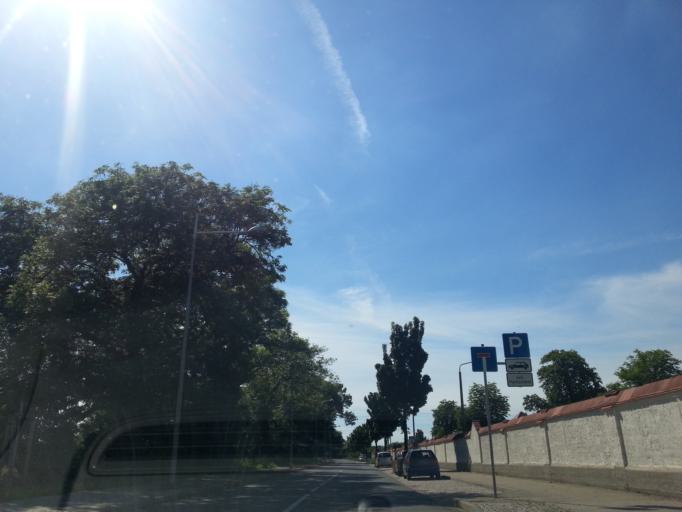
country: DE
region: Saxony
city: Dresden
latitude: 51.0687
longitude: 13.7142
